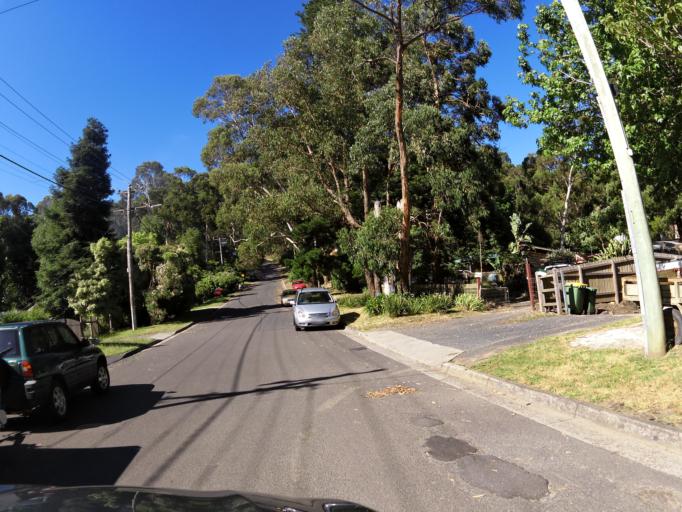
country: AU
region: Victoria
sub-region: Yarra Ranges
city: Tremont
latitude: -37.8951
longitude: 145.3386
